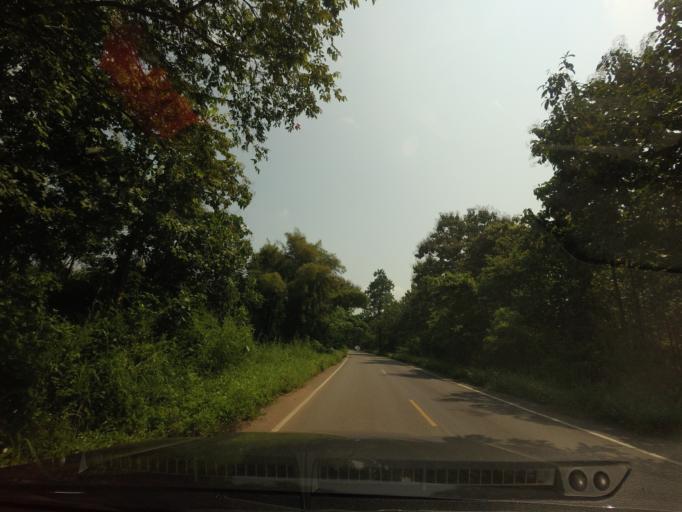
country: TH
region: Nan
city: Nan
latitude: 18.8508
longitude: 100.7829
